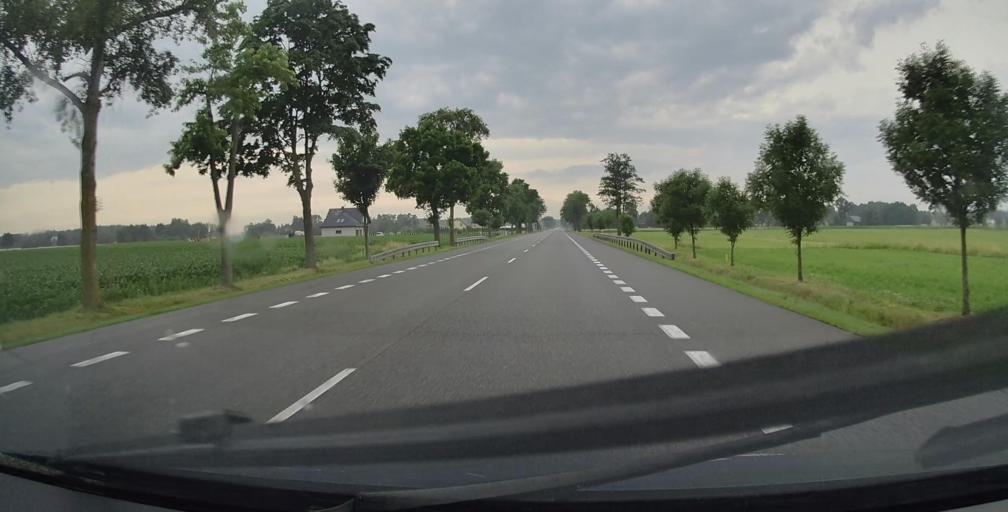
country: PL
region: Masovian Voivodeship
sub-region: Powiat siedlecki
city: Zbuczyn
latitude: 52.0710
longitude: 22.5126
